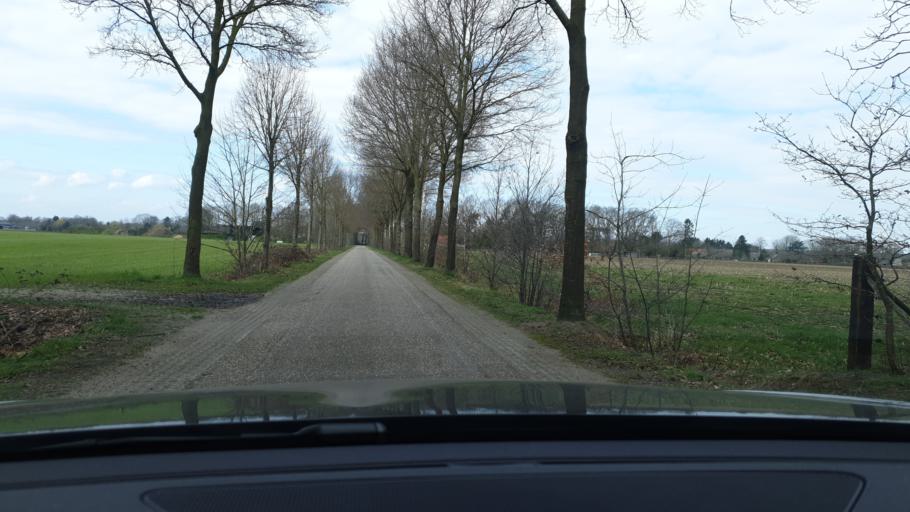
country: NL
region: North Brabant
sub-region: Gemeente Bladel en Netersel
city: Bladel
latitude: 51.3983
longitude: 5.2512
